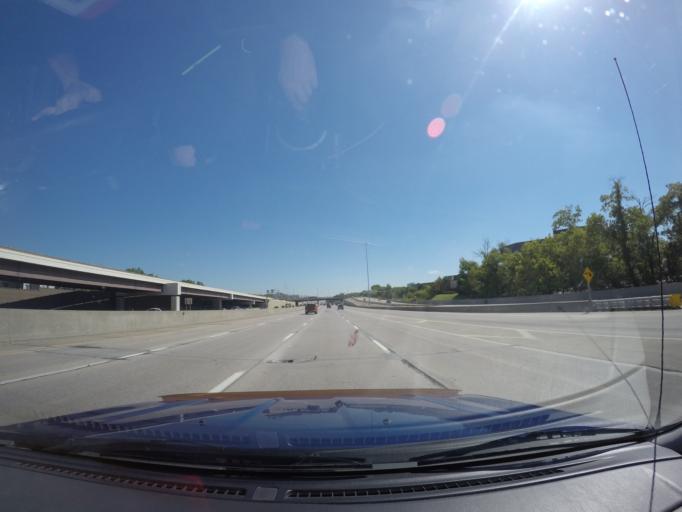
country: US
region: Kansas
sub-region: Johnson County
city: Lenexa
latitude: 38.9345
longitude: -94.6905
